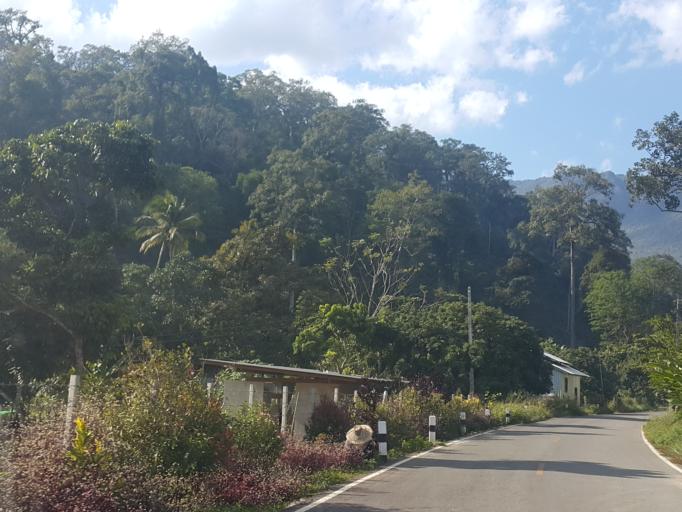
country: TH
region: Chiang Mai
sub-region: Amphoe Chiang Dao
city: Chiang Dao
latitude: 19.4067
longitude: 98.9252
